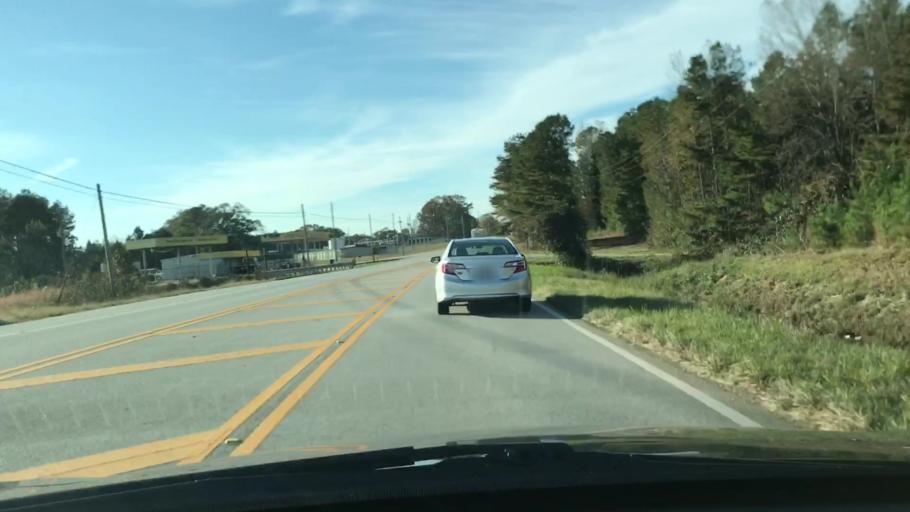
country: US
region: Alabama
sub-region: Cleburne County
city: Heflin
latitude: 33.6476
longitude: -85.5099
